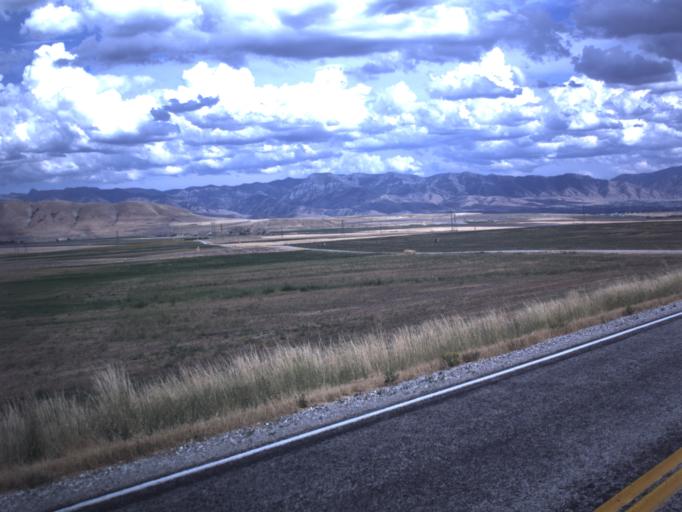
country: US
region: Utah
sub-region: Cache County
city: Benson
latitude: 41.8886
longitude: -112.0371
